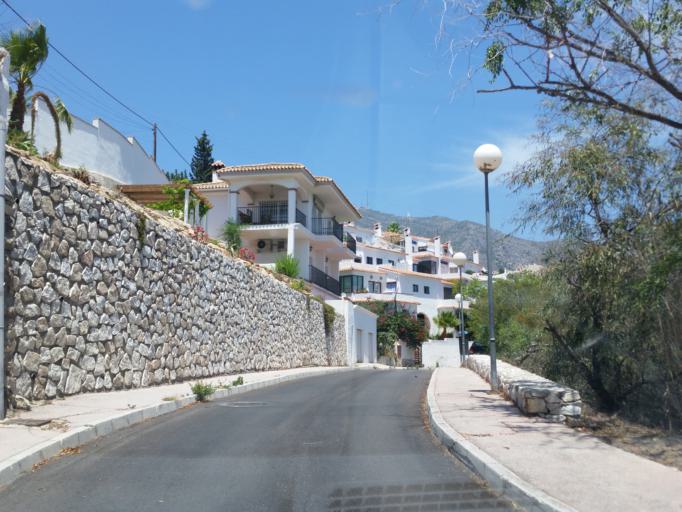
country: ES
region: Andalusia
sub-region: Provincia de Malaga
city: Fuengirola
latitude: 36.5676
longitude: -4.6057
